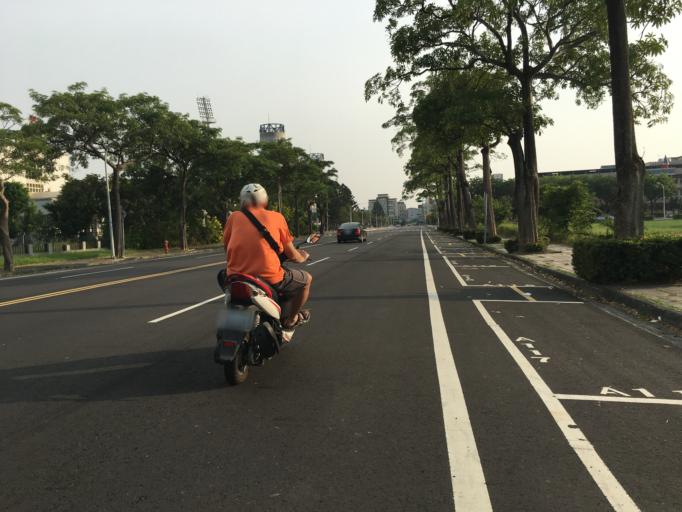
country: TW
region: Taiwan
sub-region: Chiayi
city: Taibao
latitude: 23.4593
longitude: 120.2886
